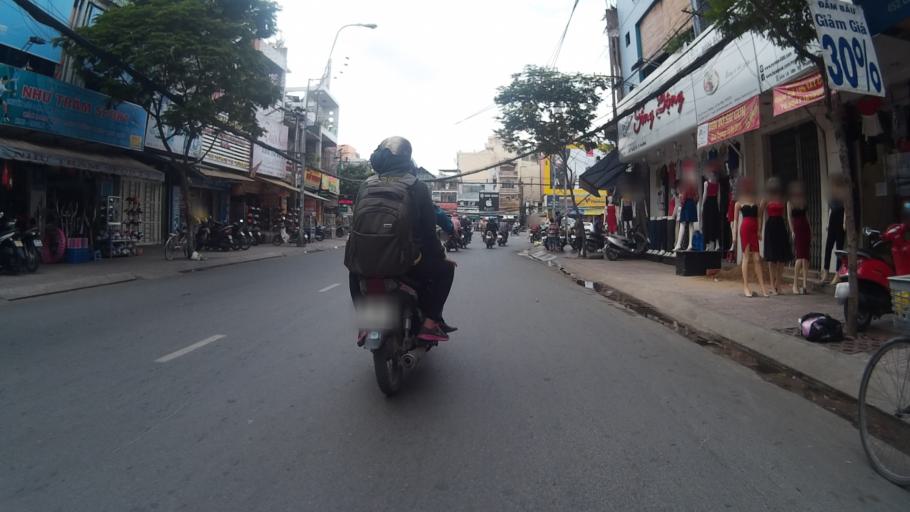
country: VN
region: Ho Chi Minh City
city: Quan Phu Nhuan
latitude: 10.7995
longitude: 106.6612
